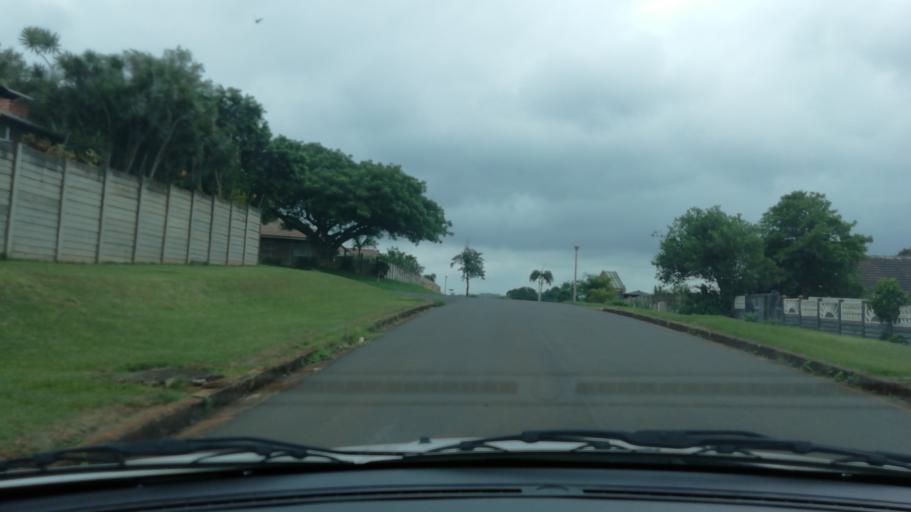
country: ZA
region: KwaZulu-Natal
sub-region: uThungulu District Municipality
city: Empangeni
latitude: -28.7631
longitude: 31.9042
